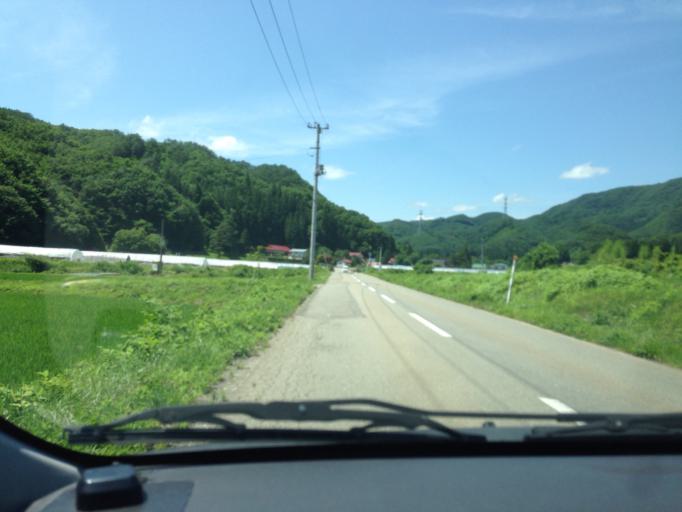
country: JP
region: Tochigi
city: Kuroiso
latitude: 37.2105
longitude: 139.7570
